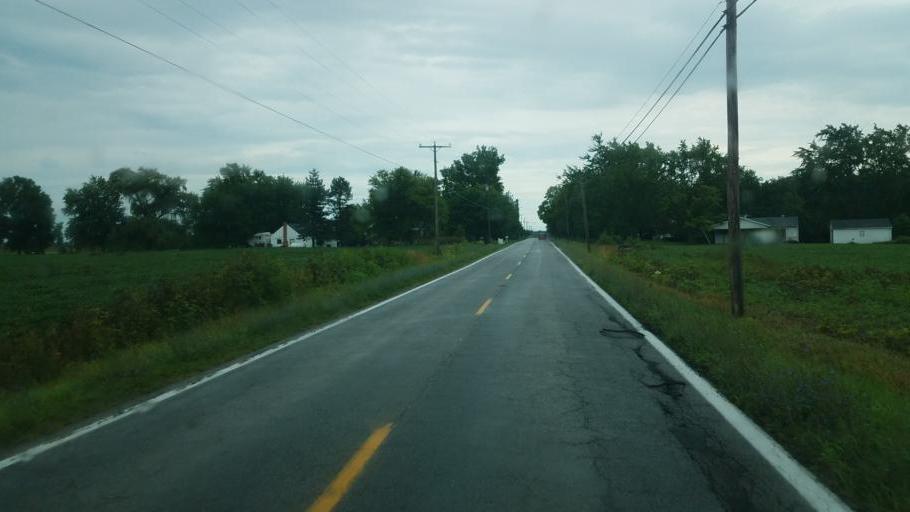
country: US
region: Ohio
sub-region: Marion County
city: Marion
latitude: 40.5562
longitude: -83.0815
